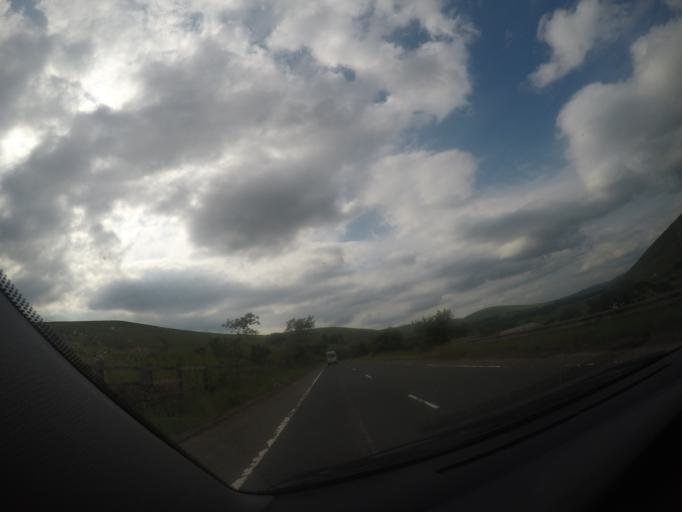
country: GB
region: Scotland
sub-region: South Lanarkshire
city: Douglas
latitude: 55.4697
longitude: -3.6877
